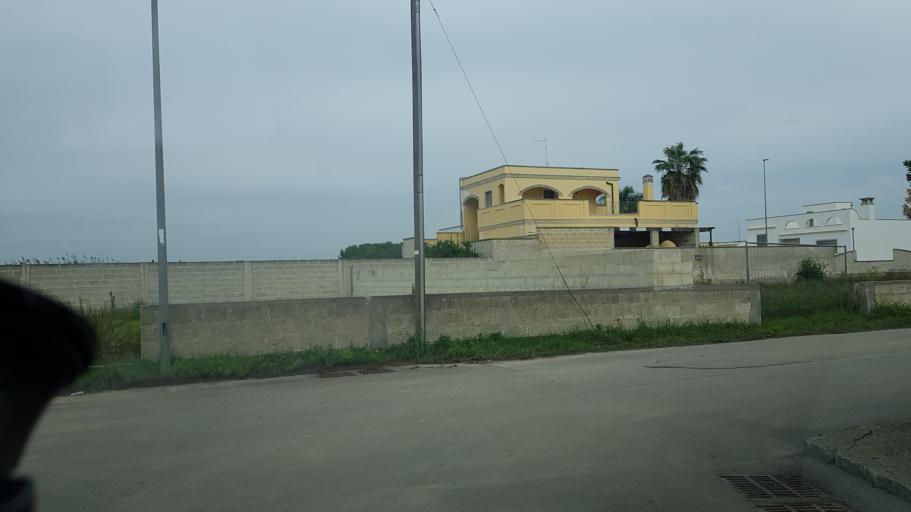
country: IT
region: Apulia
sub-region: Provincia di Lecce
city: Guagnano
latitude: 40.4037
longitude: 17.9407
